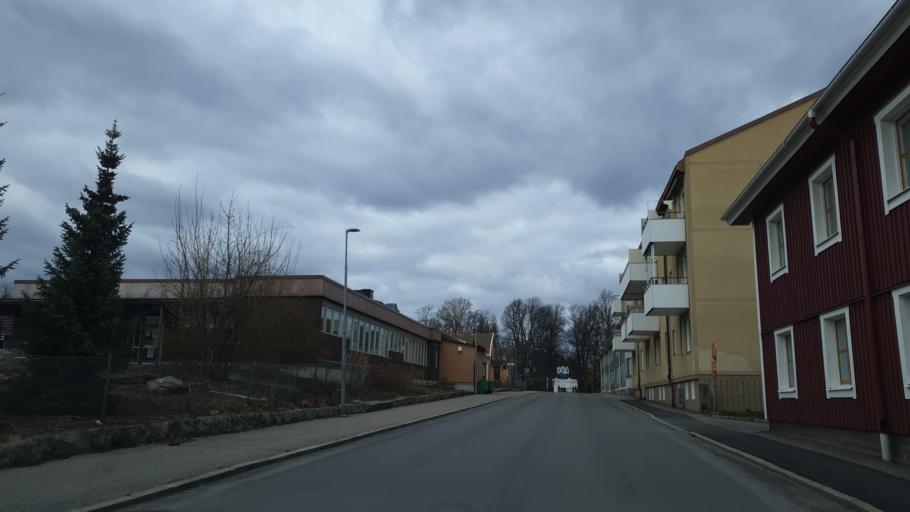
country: SE
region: OErebro
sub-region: Nora Kommun
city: Nora
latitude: 59.5209
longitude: 15.0385
